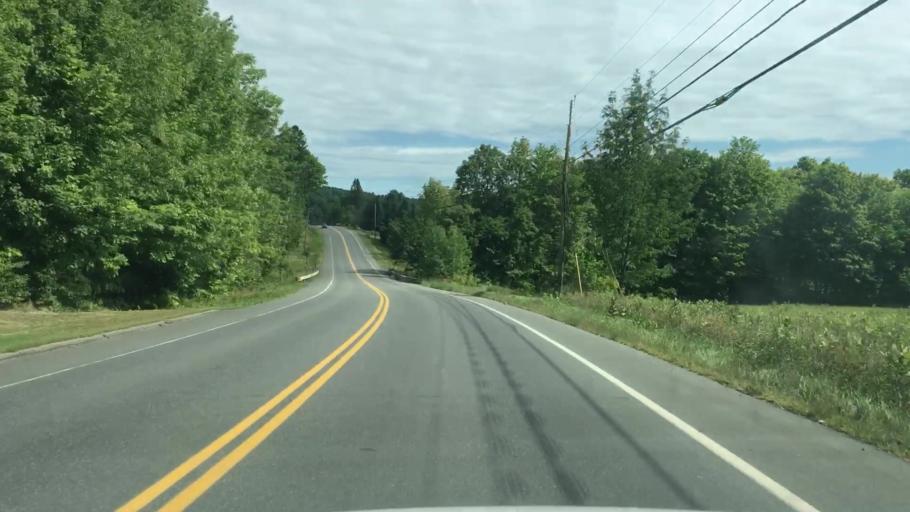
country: US
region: Maine
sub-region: Piscataquis County
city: Dover-Foxcroft
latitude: 45.2023
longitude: -69.1880
